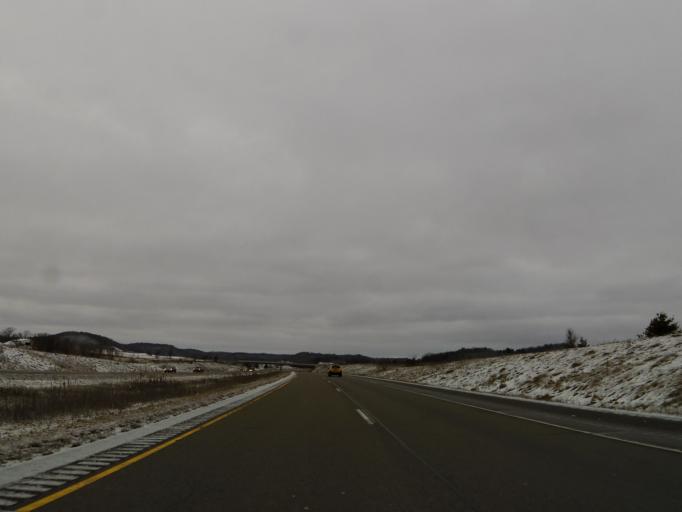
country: US
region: Wisconsin
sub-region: Jackson County
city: Black River Falls
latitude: 44.4090
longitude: -91.0341
